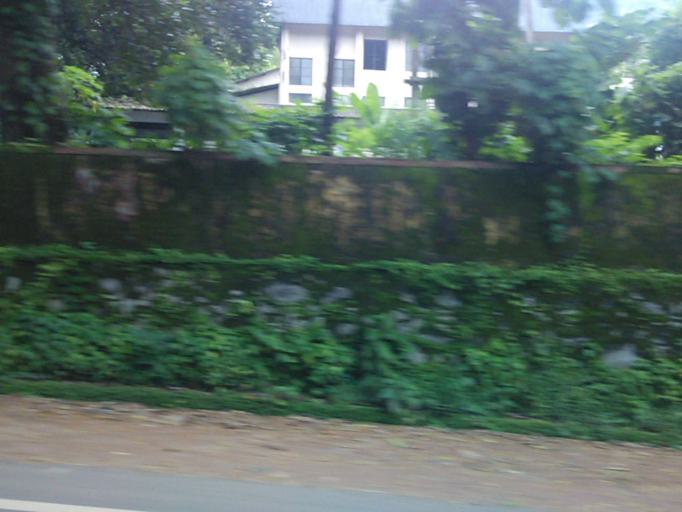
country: IN
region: Kerala
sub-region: Kozhikode
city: Kunnamangalam
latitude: 11.2931
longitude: 75.8258
